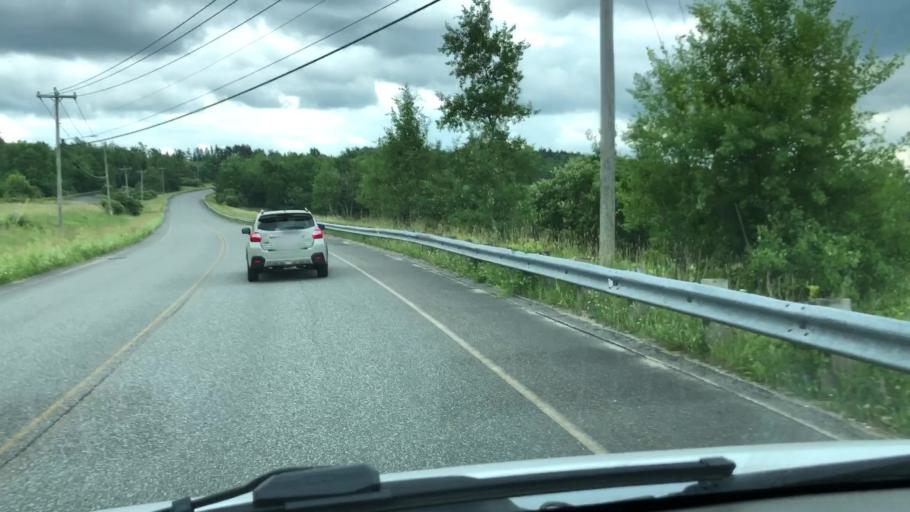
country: US
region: Massachusetts
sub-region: Berkshire County
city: Hinsdale
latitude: 42.5231
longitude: -73.0600
